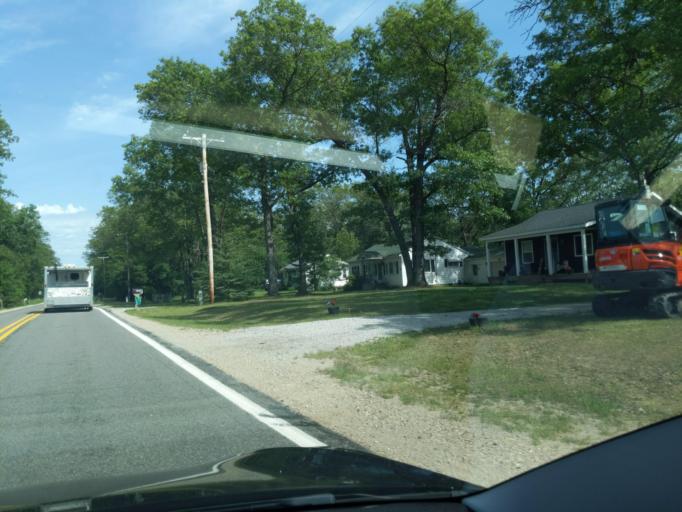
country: US
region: Michigan
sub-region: Muskegon County
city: Lakewood Club
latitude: 43.4072
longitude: -86.2686
